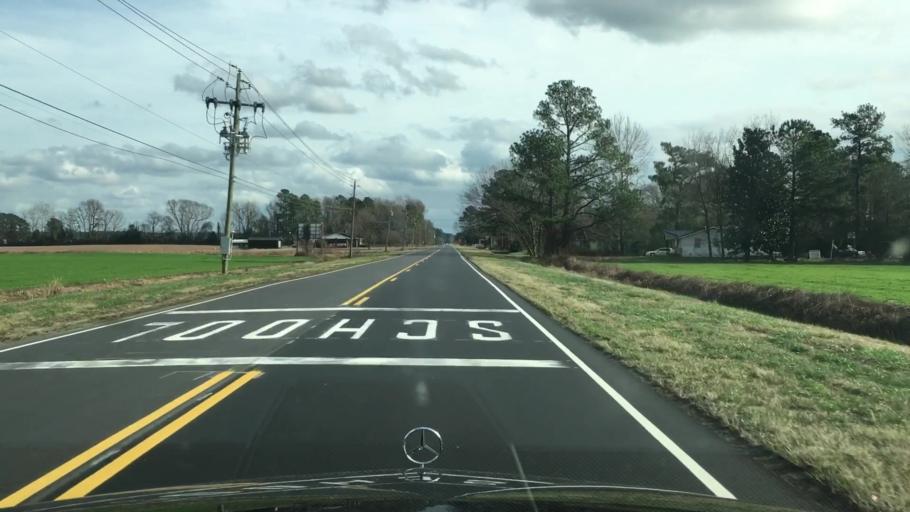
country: US
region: North Carolina
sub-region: Duplin County
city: Warsaw
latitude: 34.9827
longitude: -78.0368
